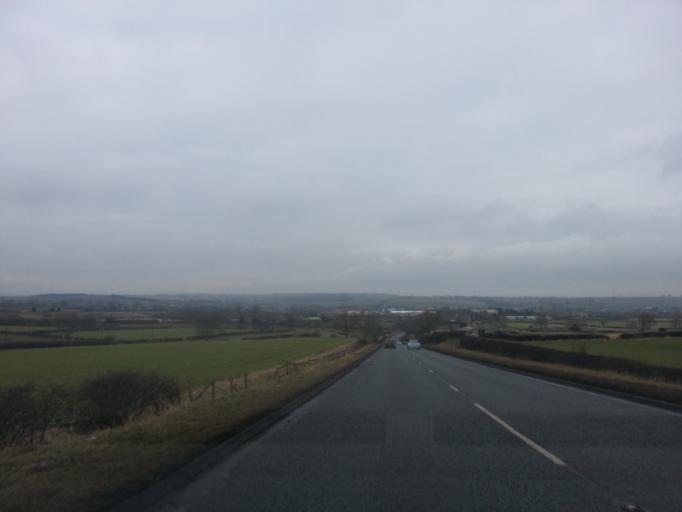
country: GB
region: England
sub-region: County Durham
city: Bishop Auckland
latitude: 54.6191
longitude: -1.7046
